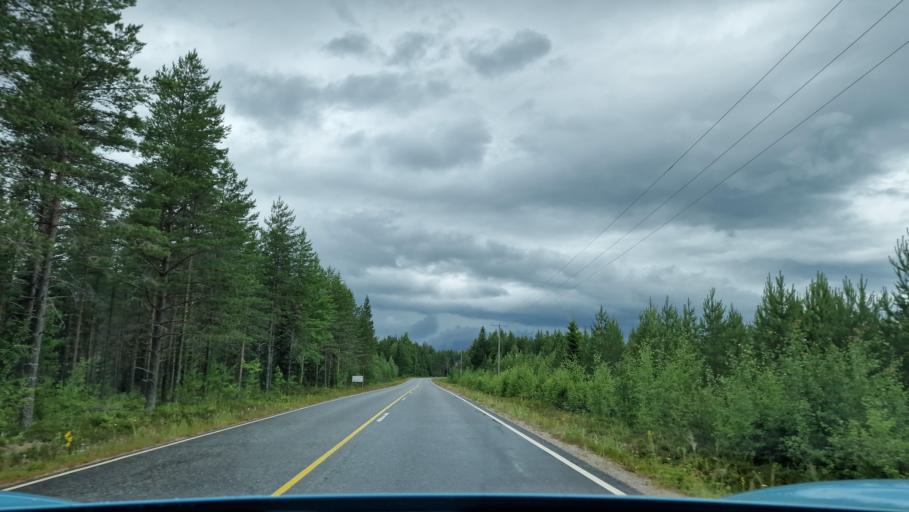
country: FI
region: Southern Ostrobothnia
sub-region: Jaerviseutu
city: Soini
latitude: 62.7379
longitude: 24.4194
